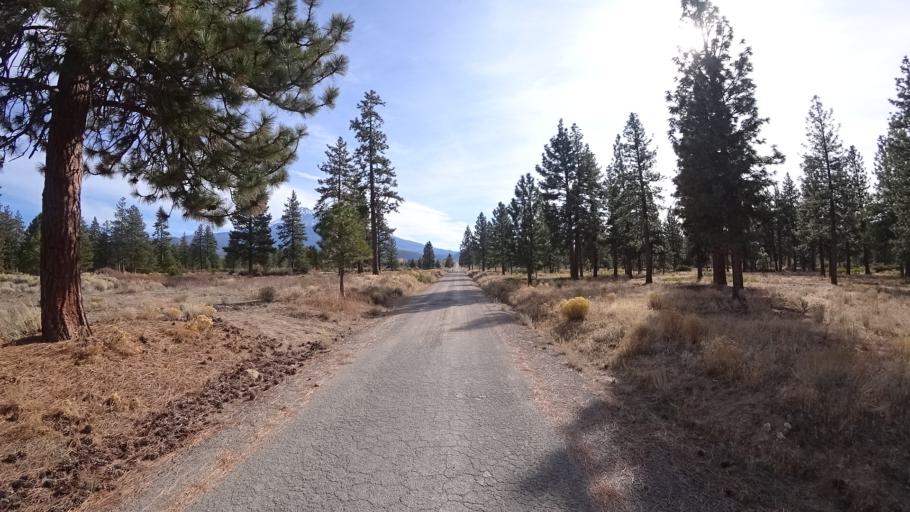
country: US
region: California
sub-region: Siskiyou County
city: Weed
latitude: 41.4921
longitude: -122.3730
